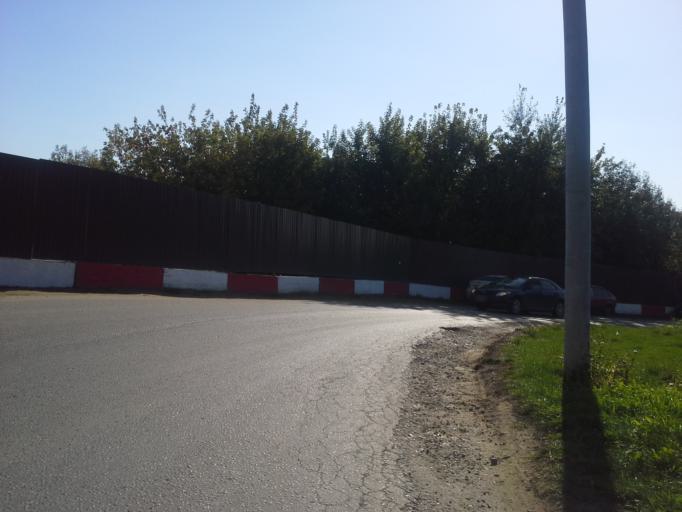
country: RU
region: Moskovskaya
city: Kommunarka
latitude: 55.5659
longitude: 37.4845
